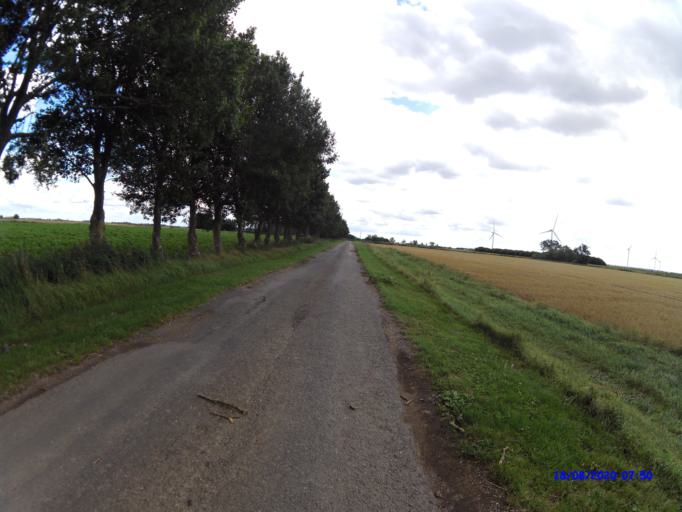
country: GB
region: England
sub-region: Cambridgeshire
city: Whittlesey
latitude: 52.5204
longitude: -0.0947
